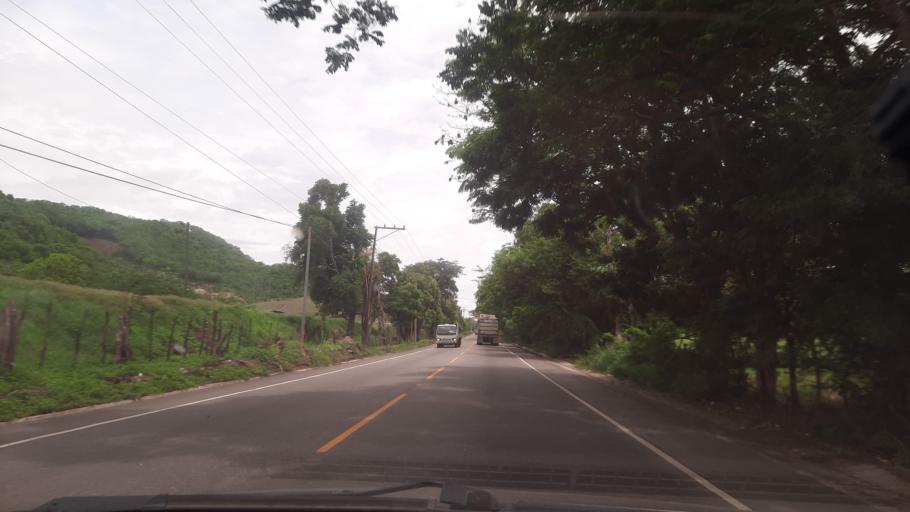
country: GT
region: Zacapa
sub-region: Municipio de Zacapa
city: Gualan
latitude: 15.0885
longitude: -89.4503
